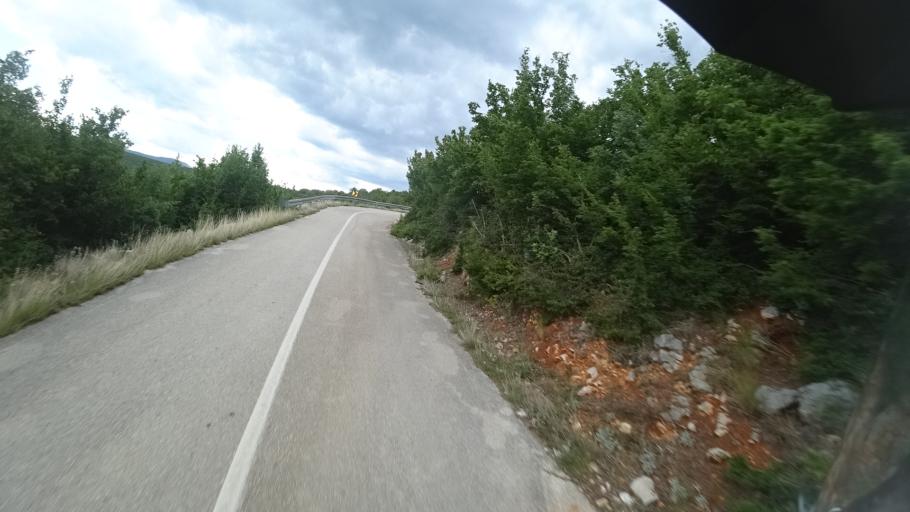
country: HR
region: Zadarska
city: Gracac
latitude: 44.1941
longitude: 15.8773
